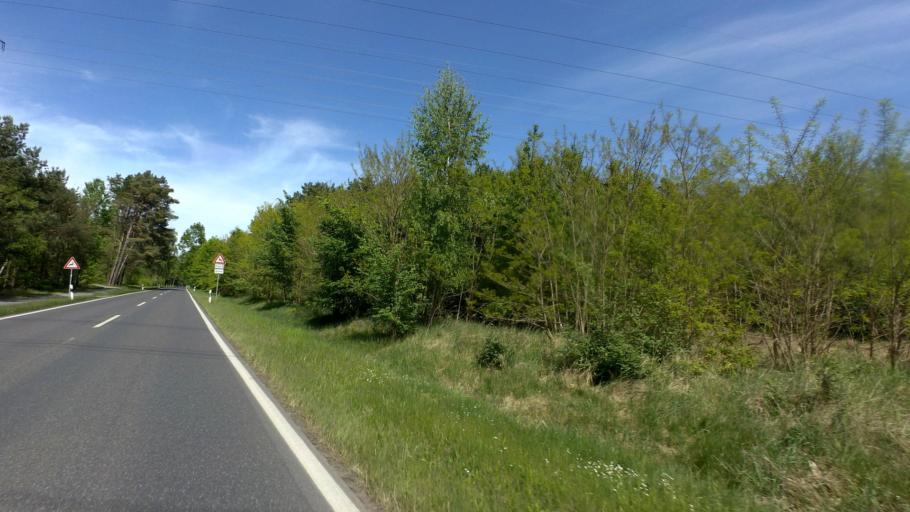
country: DE
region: Brandenburg
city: Sperenberg
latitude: 52.1542
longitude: 13.3655
